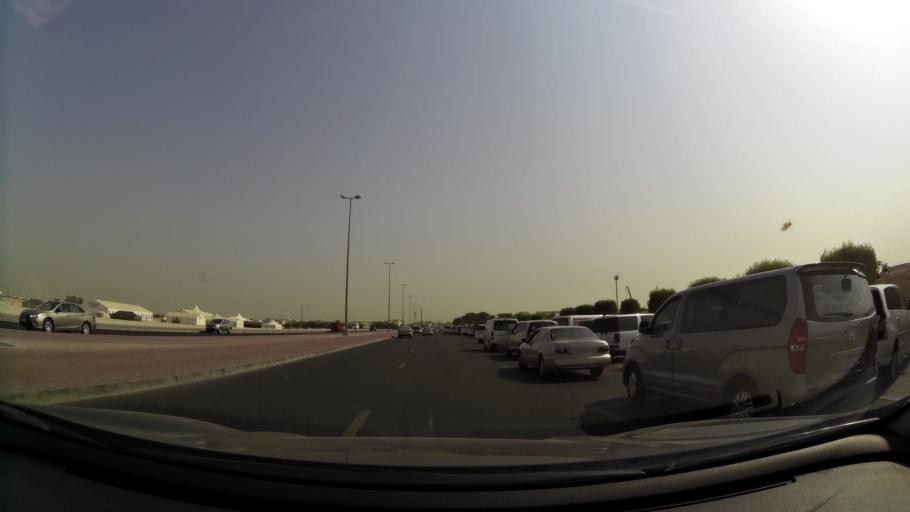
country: KW
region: Al Asimah
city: Ar Rabiyah
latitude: 29.2796
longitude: 47.9193
